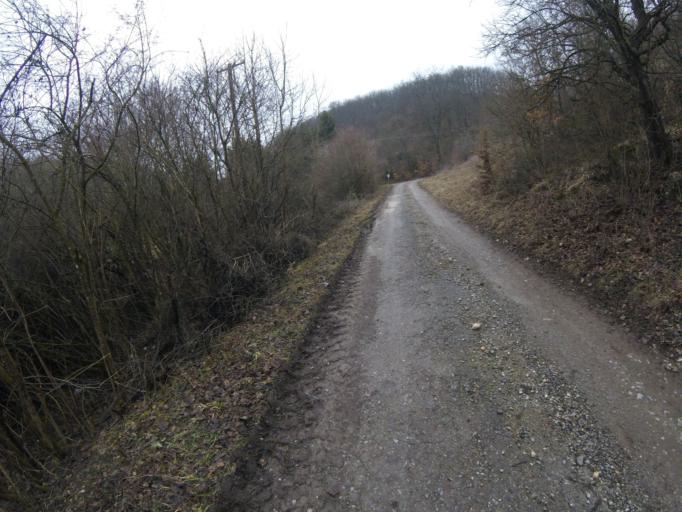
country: HU
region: Borsod-Abauj-Zemplen
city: Rudabanya
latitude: 48.4456
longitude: 20.5784
